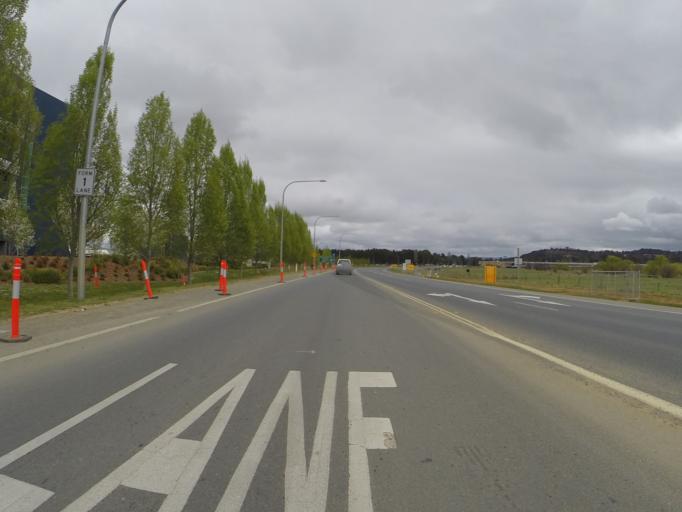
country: AU
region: Australian Capital Territory
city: Canberra
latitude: -35.2979
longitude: 149.1863
